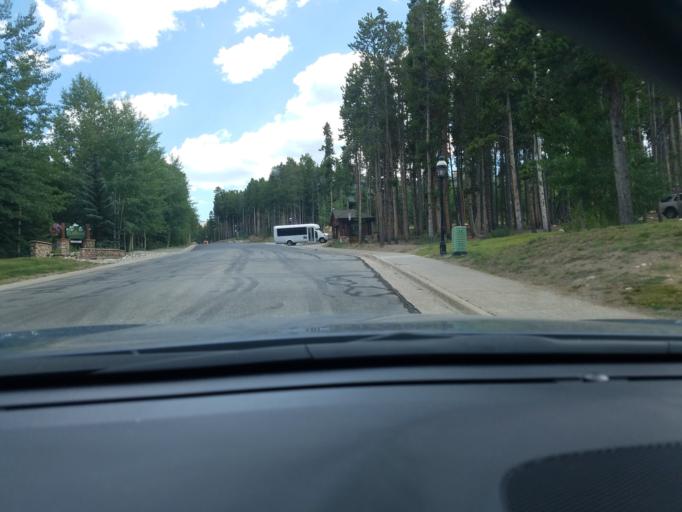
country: US
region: Colorado
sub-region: Summit County
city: Breckenridge
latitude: 39.4774
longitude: -106.0519
